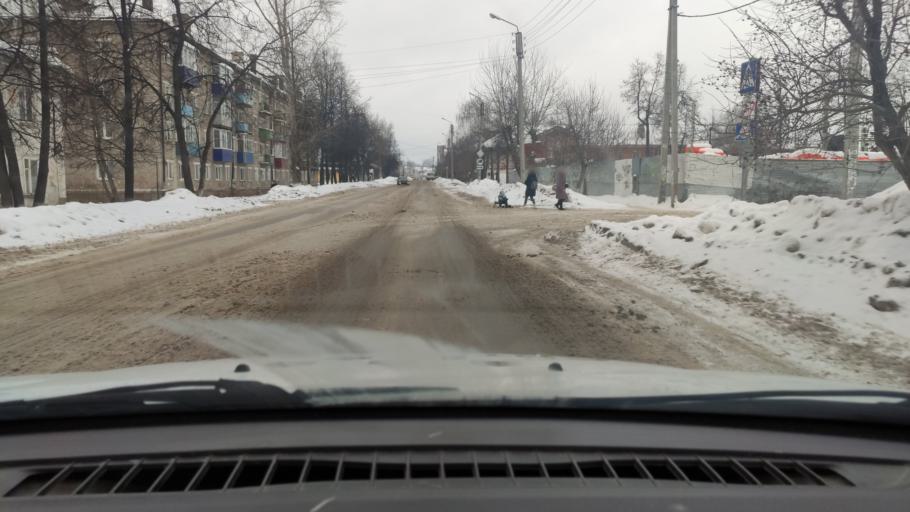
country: RU
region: Perm
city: Kungur
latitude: 57.4388
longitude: 56.9313
